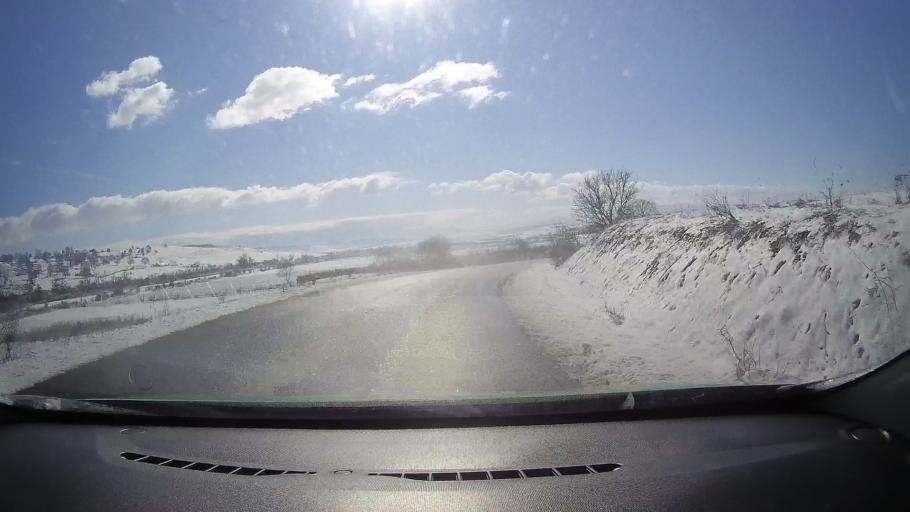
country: RO
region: Sibiu
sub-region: Comuna Rosia
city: Rosia
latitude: 45.8528
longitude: 24.3095
